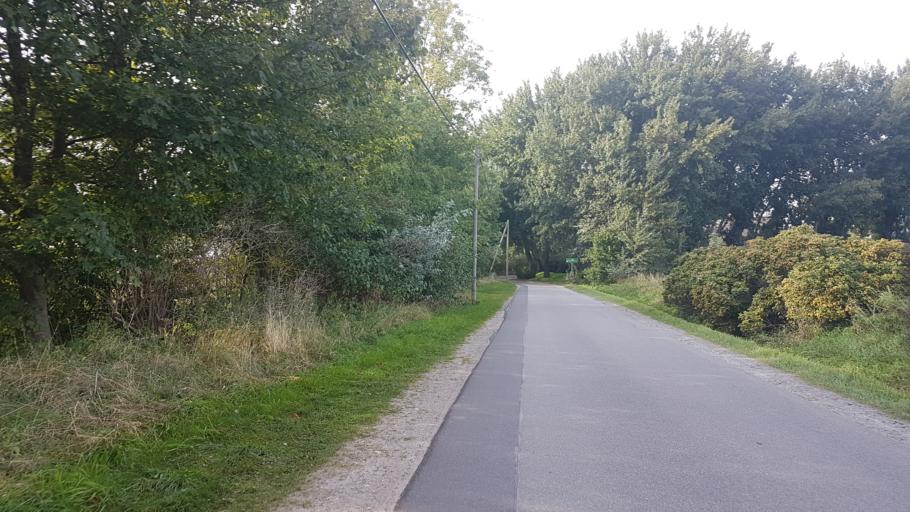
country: DE
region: Mecklenburg-Vorpommern
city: Hiddensee
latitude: 54.4601
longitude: 13.1360
